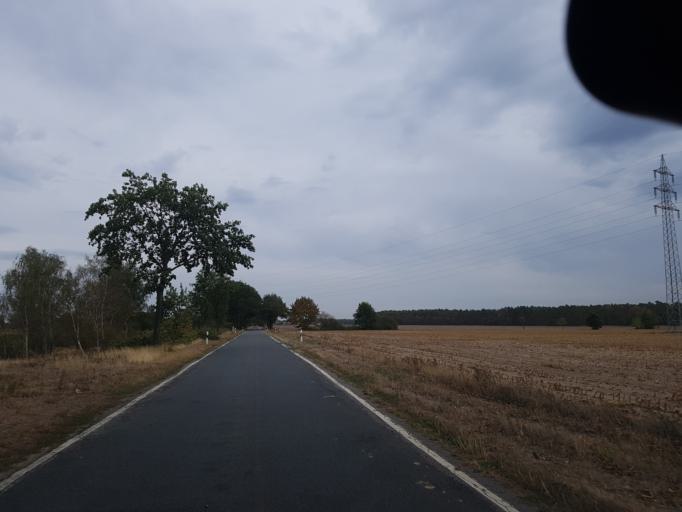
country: DE
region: Saxony-Anhalt
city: Annaburg
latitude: 51.7747
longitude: 13.0599
